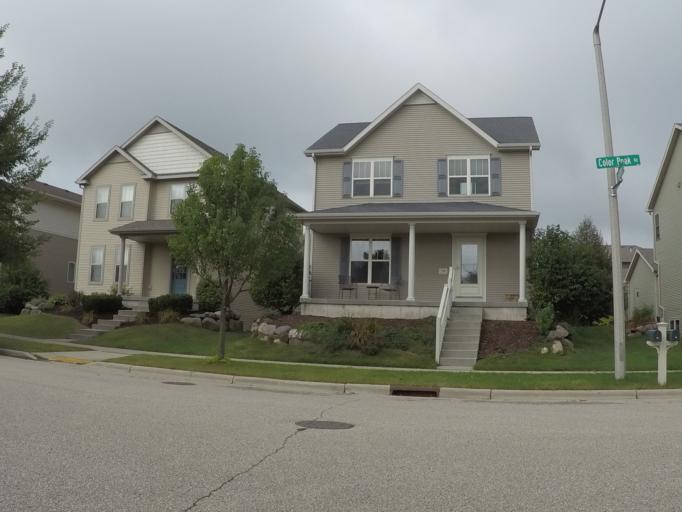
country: US
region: Wisconsin
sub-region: Dane County
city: Verona
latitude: 43.0440
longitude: -89.5400
